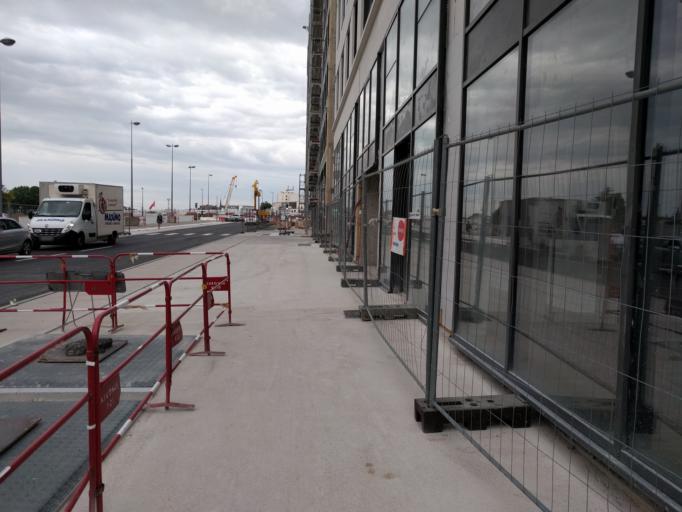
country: FR
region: Lorraine
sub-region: Departement de Meurthe-et-Moselle
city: Nancy
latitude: 48.6871
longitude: 6.1789
